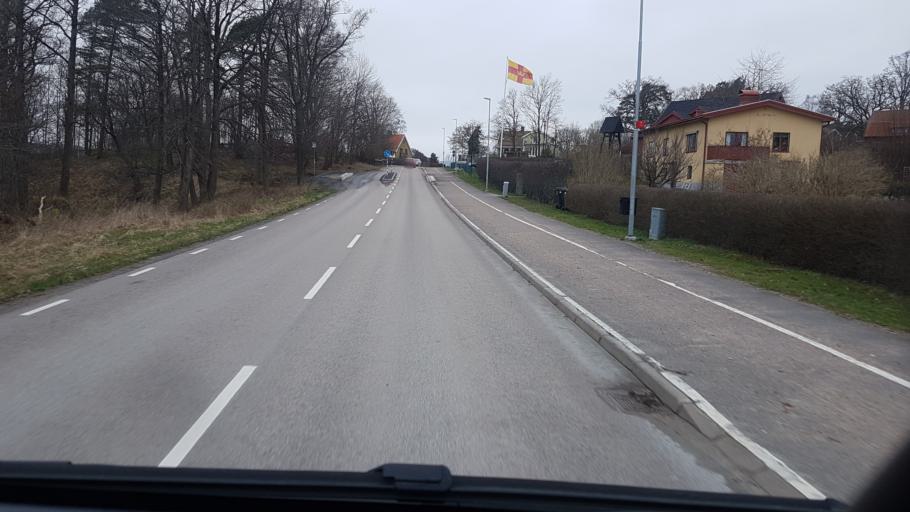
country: SE
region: Vaestra Goetaland
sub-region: Lerums Kommun
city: Lerum
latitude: 57.7706
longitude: 12.2490
